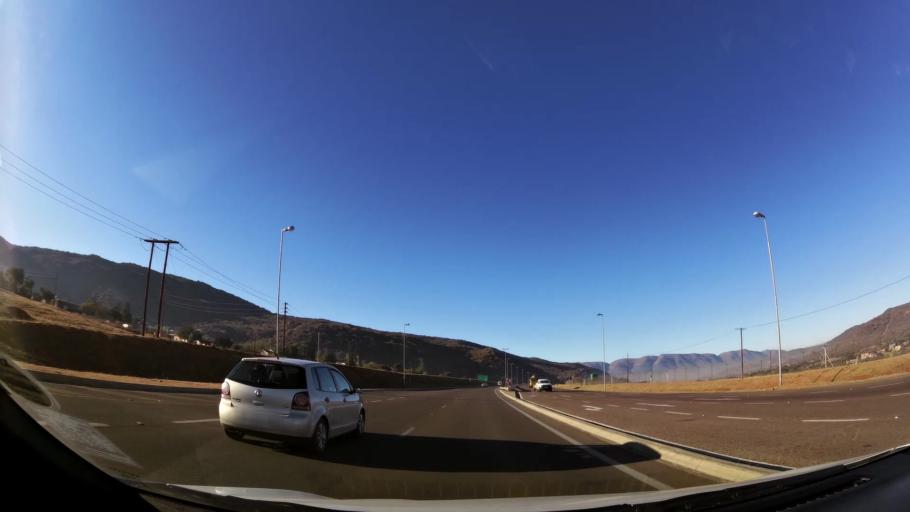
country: ZA
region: Limpopo
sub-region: Capricorn District Municipality
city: Mankoeng
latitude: -23.9199
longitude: 29.7935
